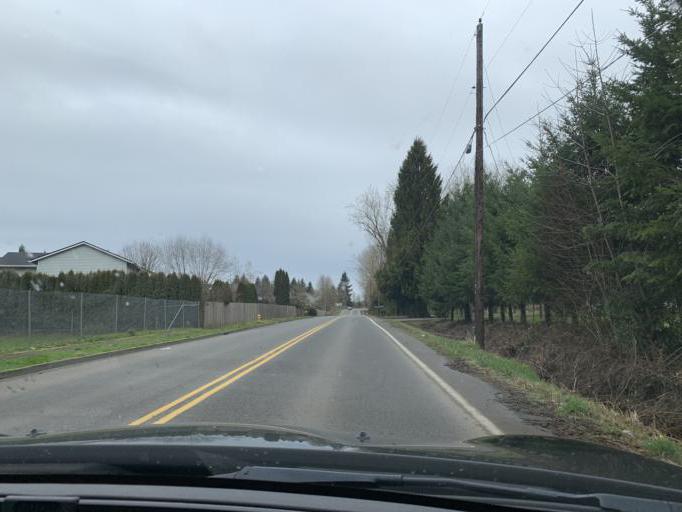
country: US
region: Washington
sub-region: Clark County
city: Barberton
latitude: 45.6862
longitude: -122.5944
